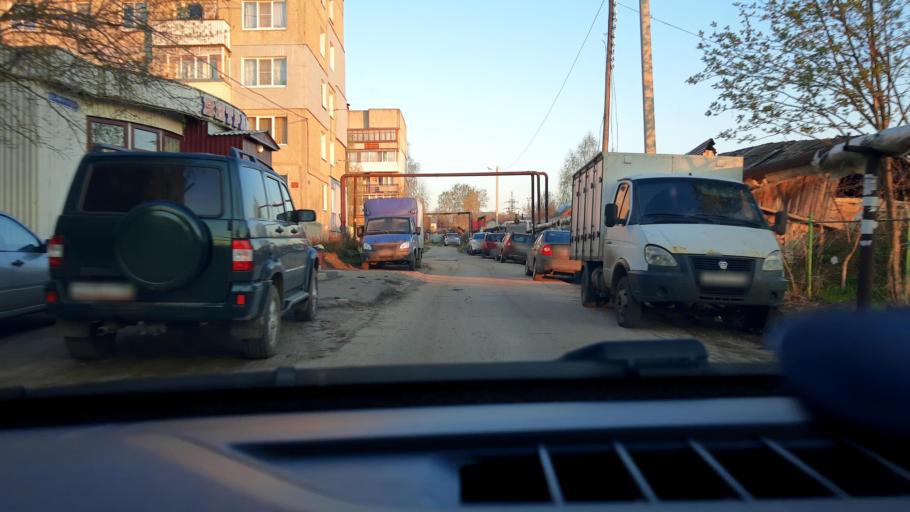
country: RU
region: Nizjnij Novgorod
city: Burevestnik
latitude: 56.1421
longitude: 43.7847
